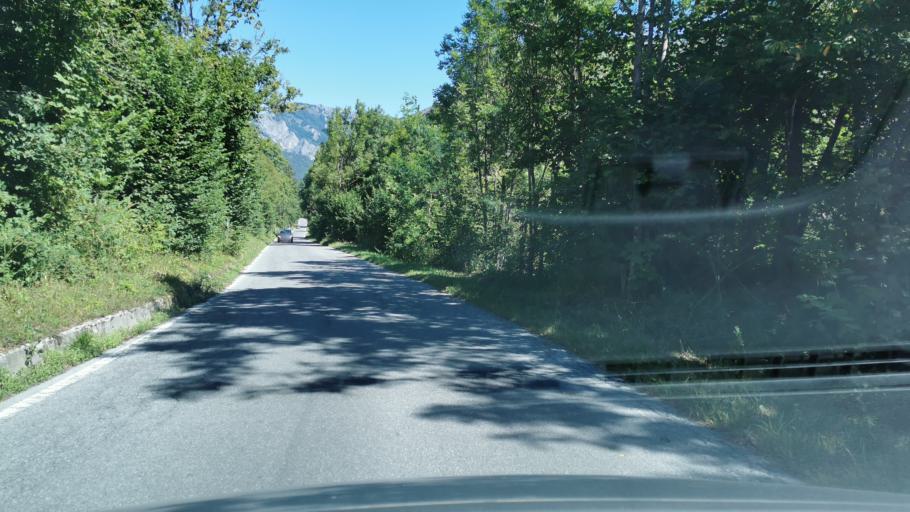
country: IT
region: Piedmont
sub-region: Provincia di Cuneo
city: Entracque
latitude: 44.2342
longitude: 7.3921
